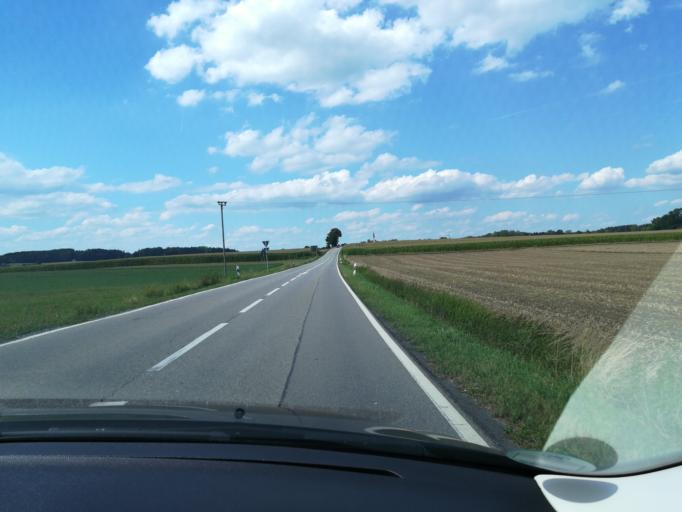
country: DE
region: Bavaria
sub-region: Upper Bavaria
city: Assling
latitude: 47.9668
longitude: 11.9621
